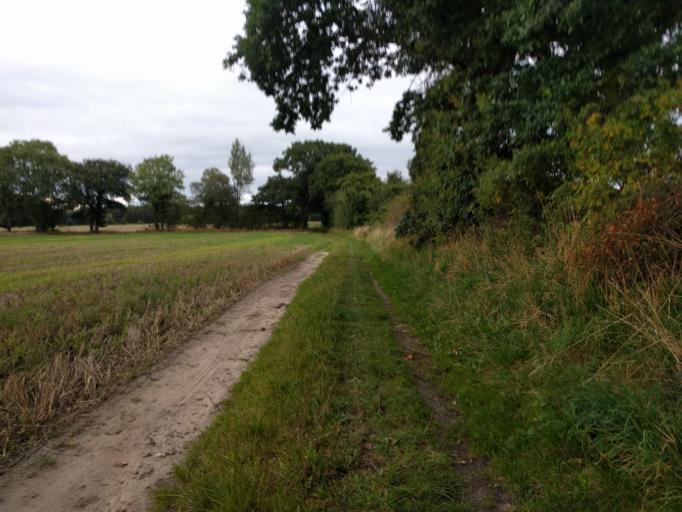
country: DK
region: South Denmark
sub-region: Kerteminde Kommune
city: Munkebo
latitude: 55.4293
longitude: 10.5213
